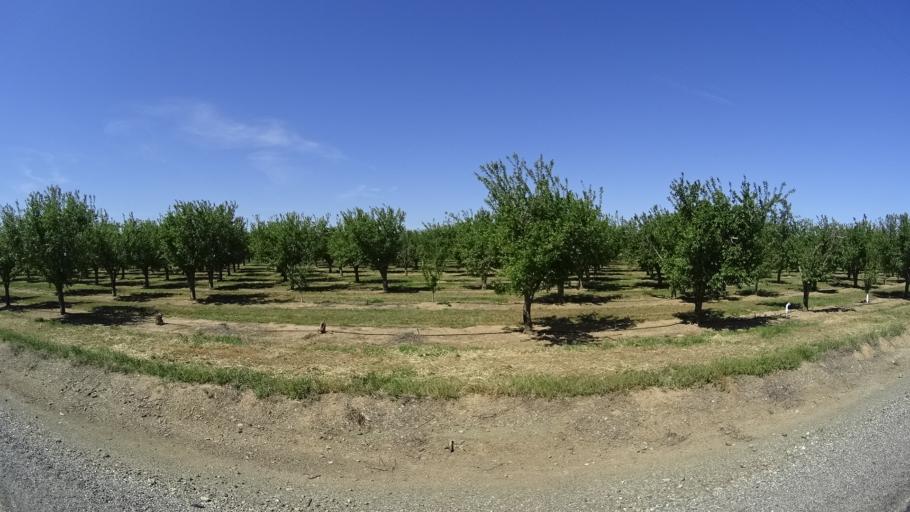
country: US
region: California
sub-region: Glenn County
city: Orland
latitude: 39.6768
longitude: -122.1404
